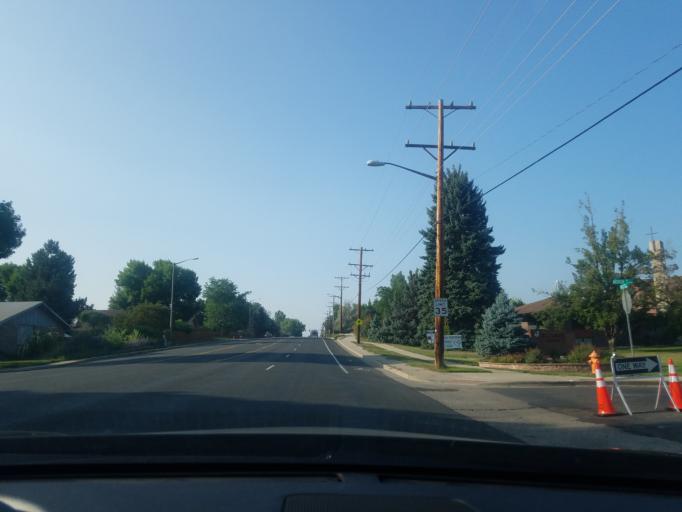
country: US
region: Colorado
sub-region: Larimer County
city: Loveland
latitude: 40.4263
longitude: -105.0967
